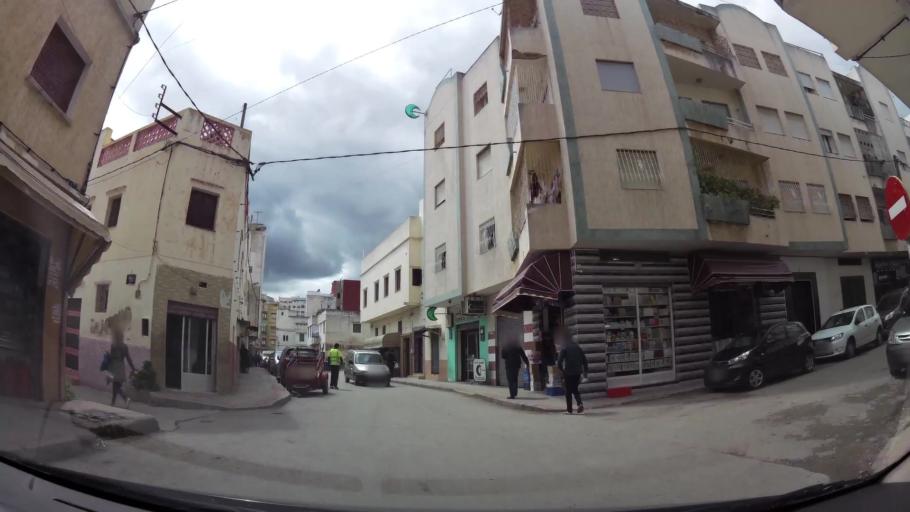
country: MA
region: Tanger-Tetouan
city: Tetouan
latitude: 35.5750
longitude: -5.3568
